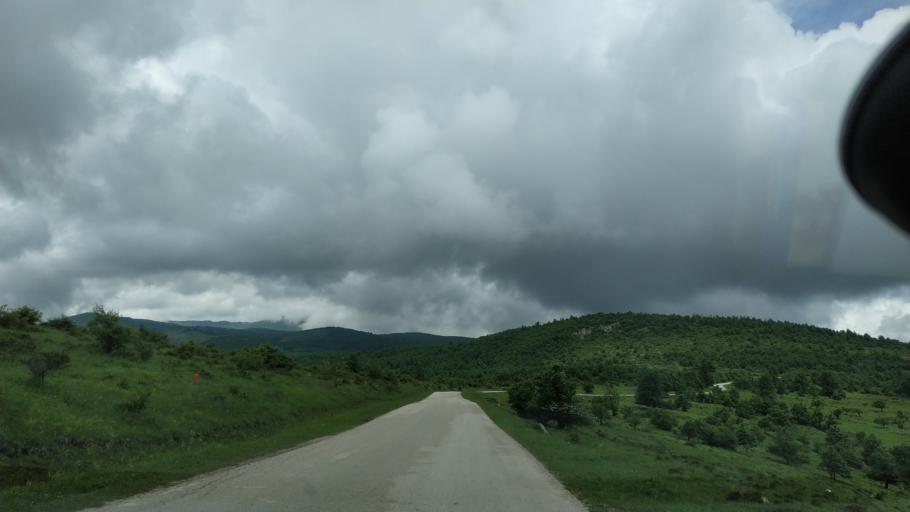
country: RS
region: Central Serbia
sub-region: Zajecarski Okrug
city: Soko Banja
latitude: 43.7109
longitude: 21.9401
